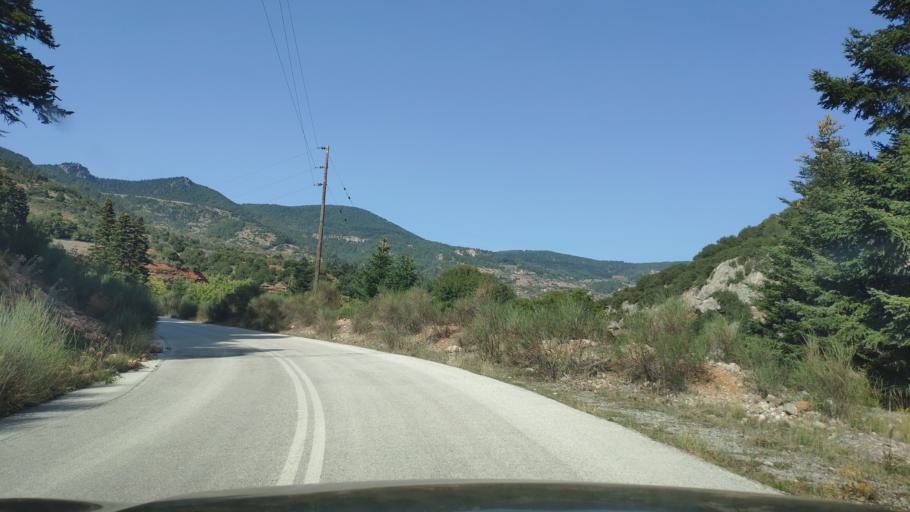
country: GR
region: West Greece
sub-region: Nomos Achaias
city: Aiyira
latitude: 37.9776
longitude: 22.3542
